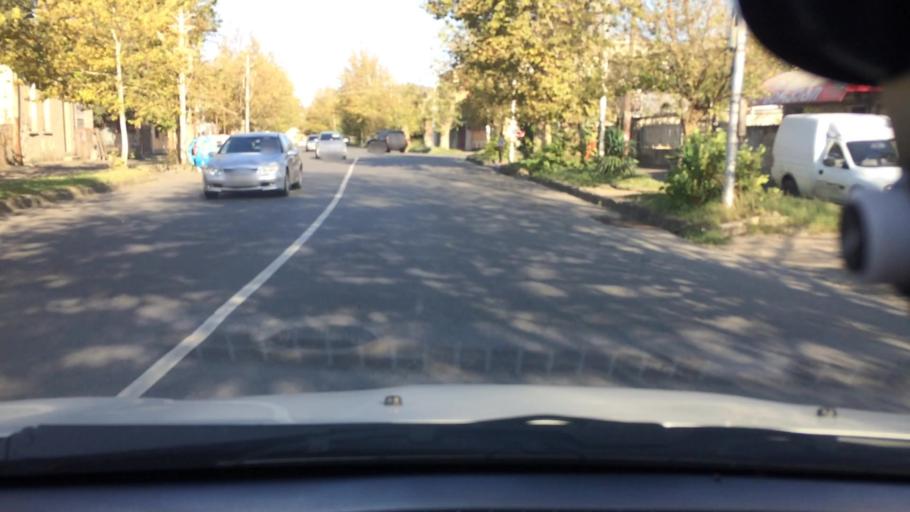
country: GE
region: Imereti
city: Kutaisi
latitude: 42.2678
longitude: 42.7167
